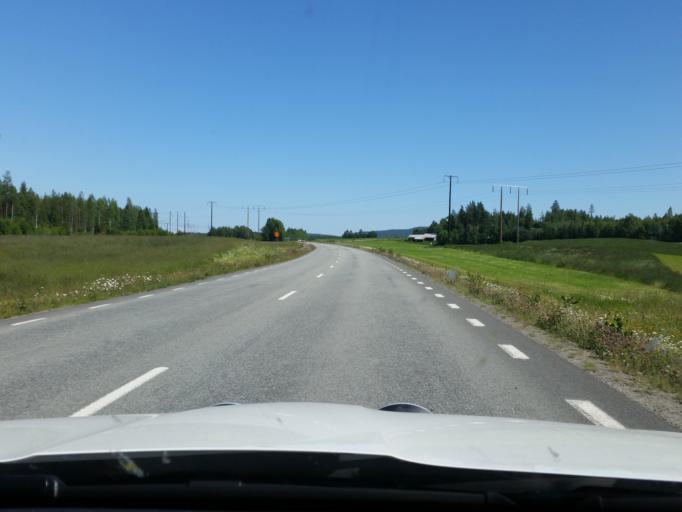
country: SE
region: Norrbotten
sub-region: Alvsbyns Kommun
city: AElvsbyn
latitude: 65.6677
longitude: 20.9071
